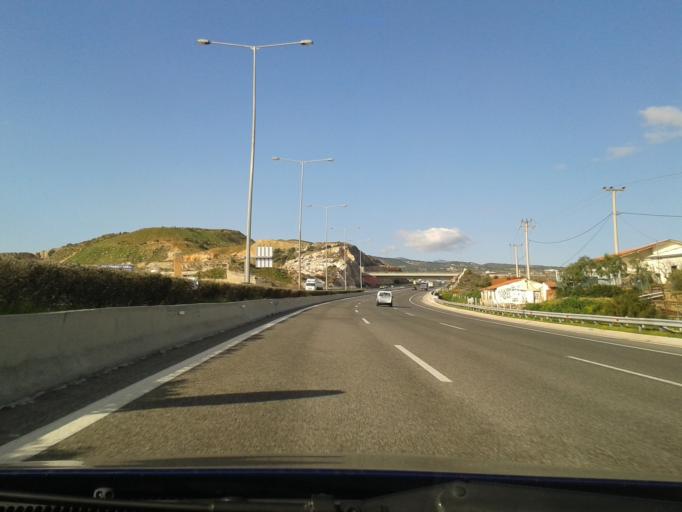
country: GR
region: Attica
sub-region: Nomarchia Dytikis Attikis
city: Megara
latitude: 37.9818
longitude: 23.3374
